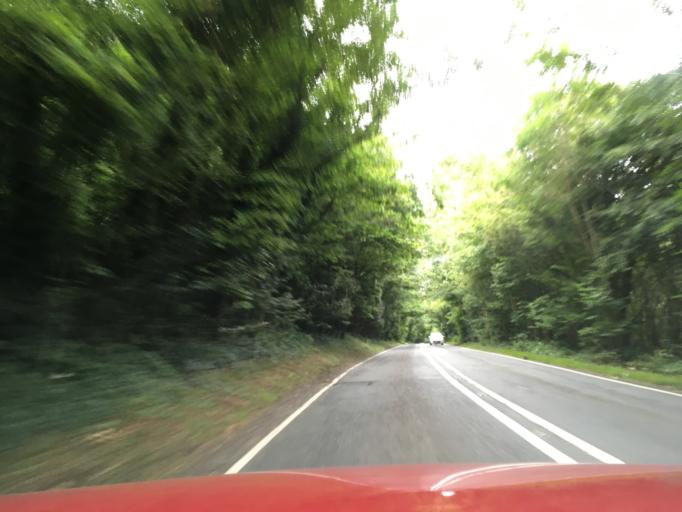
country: GB
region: England
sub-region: Hampshire
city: Four Marks
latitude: 51.0215
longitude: -1.0252
